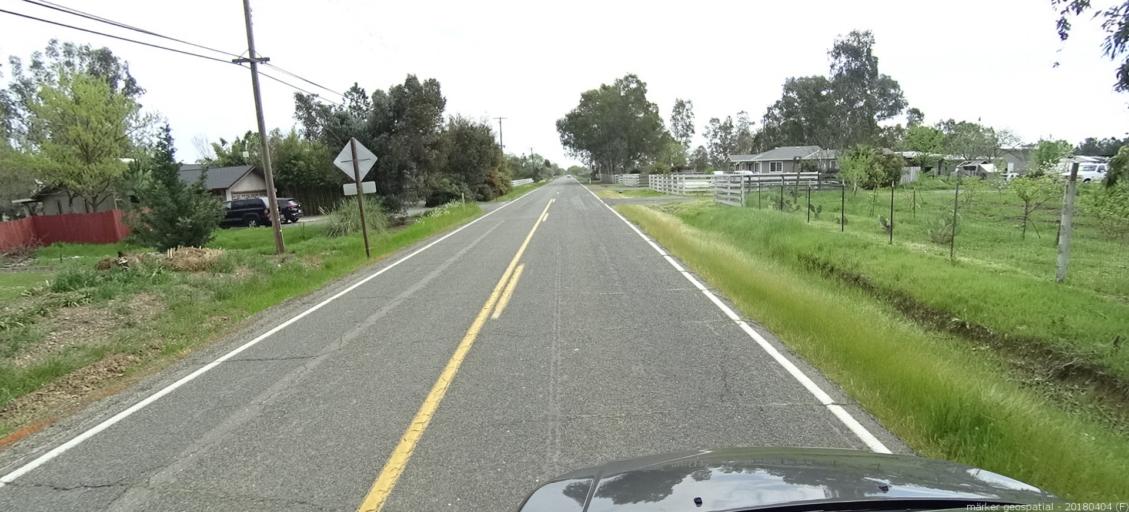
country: US
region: California
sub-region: Sacramento County
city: Herald
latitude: 38.2625
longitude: -121.2626
